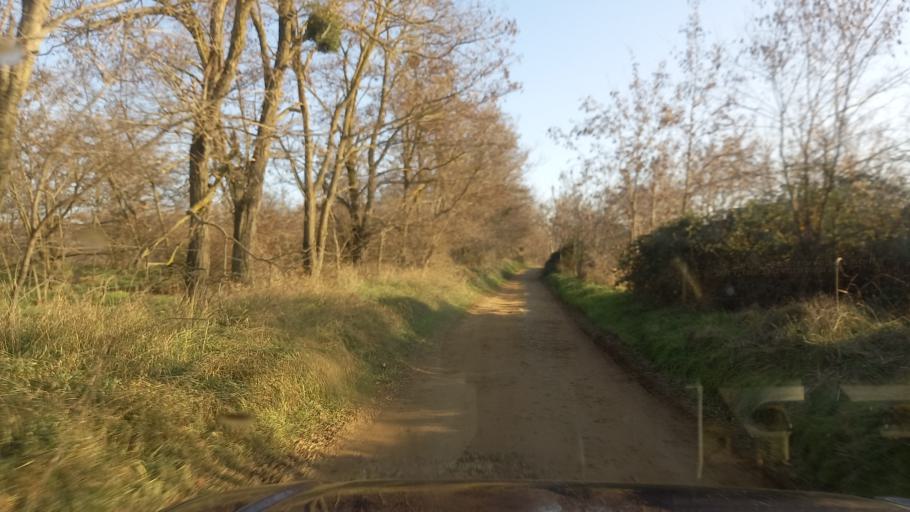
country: RU
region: Krasnodarskiy
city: Il'skiy
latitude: 44.8090
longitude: 38.5881
